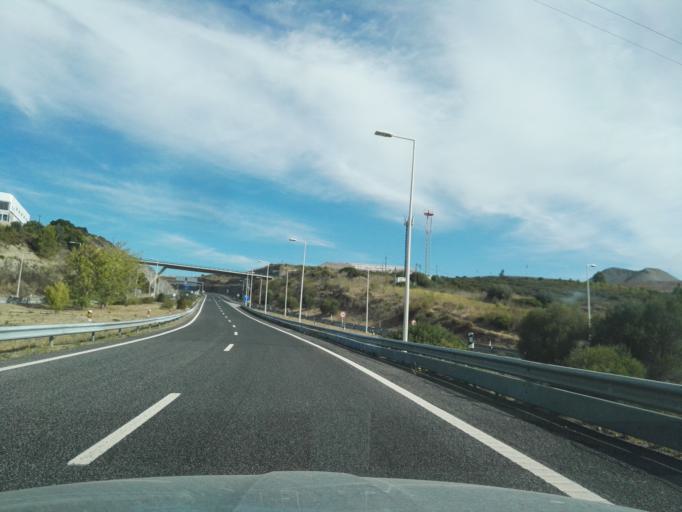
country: PT
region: Lisbon
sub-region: Vila Franca de Xira
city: Vialonga
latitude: 38.9096
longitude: -9.0727
